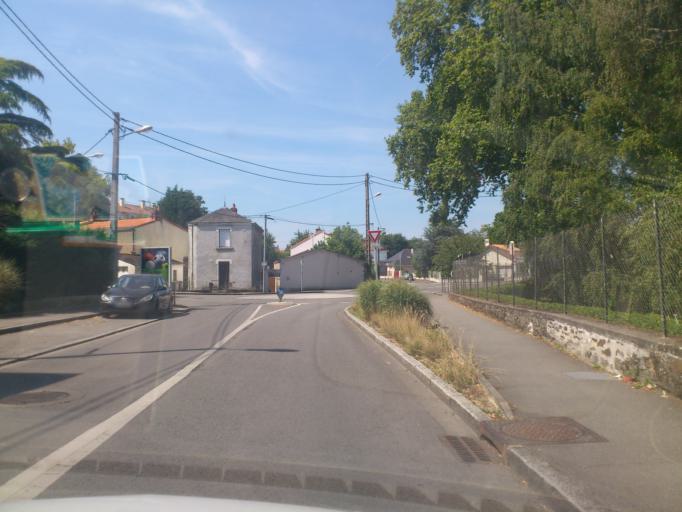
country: FR
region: Pays de la Loire
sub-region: Departement de la Loire-Atlantique
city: Reze
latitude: 47.1824
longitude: -1.5321
